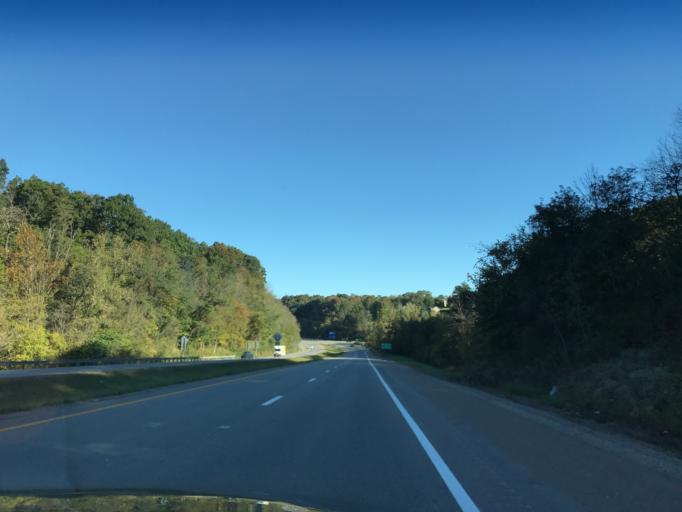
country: US
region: West Virginia
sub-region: Wood County
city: Parkersburg
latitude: 39.2573
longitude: -81.4842
